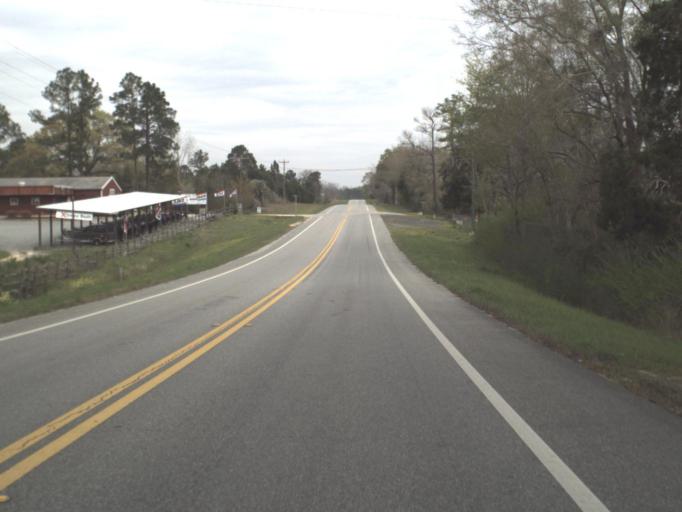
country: US
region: Florida
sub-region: Jackson County
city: Graceville
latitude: 30.9421
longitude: -85.6490
